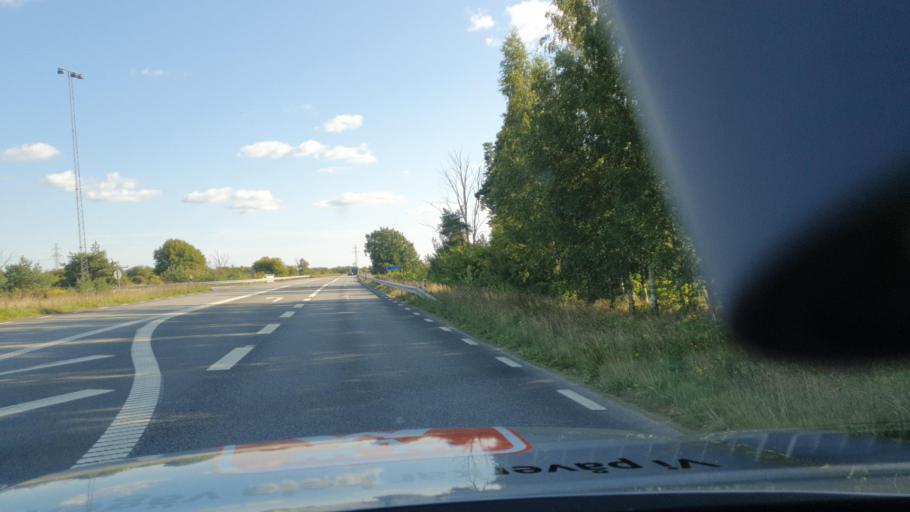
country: SE
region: Skane
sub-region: Bromolla Kommun
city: Bromoella
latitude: 56.0851
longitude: 14.4960
